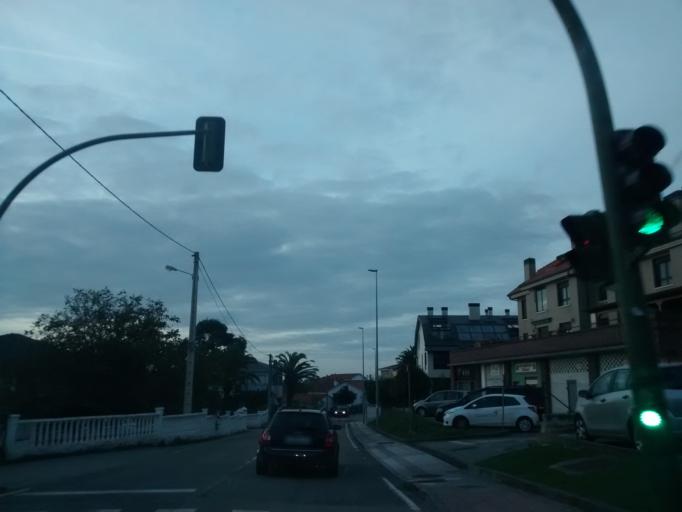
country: ES
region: Cantabria
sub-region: Provincia de Cantabria
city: Santa Cruz de Bezana
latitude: 43.4287
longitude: -3.9430
